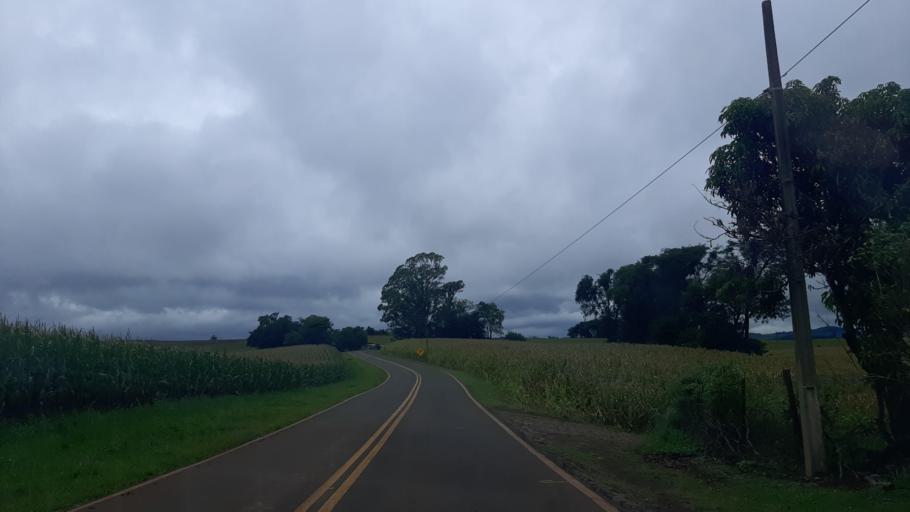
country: BR
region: Parana
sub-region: Ampere
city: Ampere
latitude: -25.9618
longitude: -53.4438
